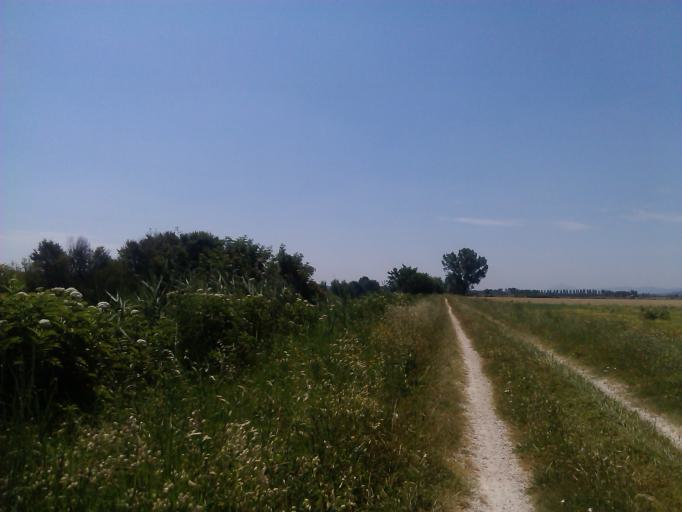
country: IT
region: Tuscany
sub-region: Province of Arezzo
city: Cesa
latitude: 43.3426
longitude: 11.8270
